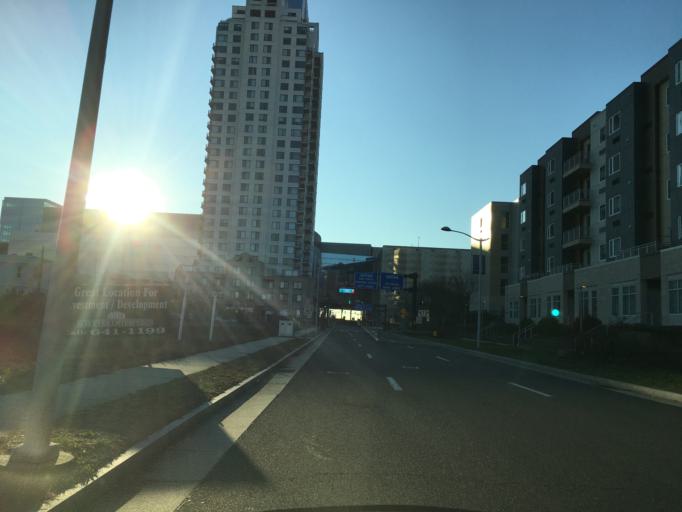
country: US
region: New Jersey
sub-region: Atlantic County
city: Atlantic City
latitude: 39.3656
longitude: -74.4176
